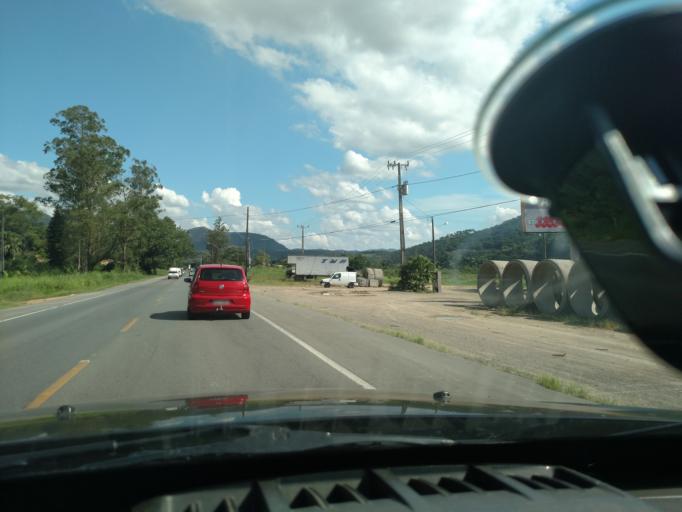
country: BR
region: Santa Catarina
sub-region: Rodeio
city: Gavea
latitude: -27.0019
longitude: -49.3750
